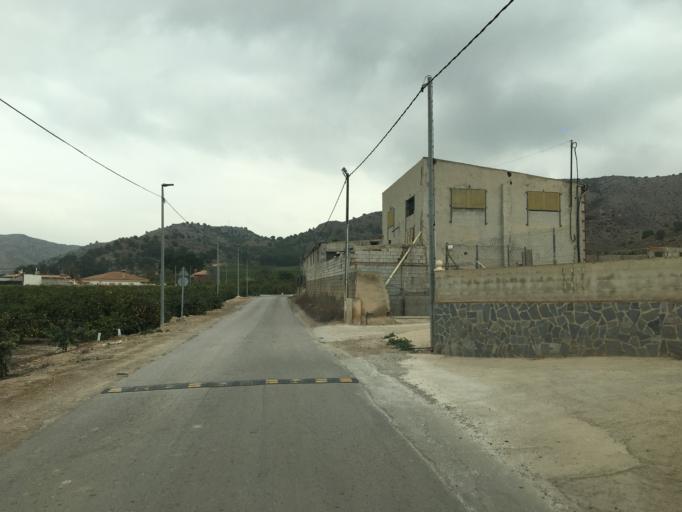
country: ES
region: Murcia
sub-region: Murcia
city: Santomera
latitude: 38.0774
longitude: -1.0465
